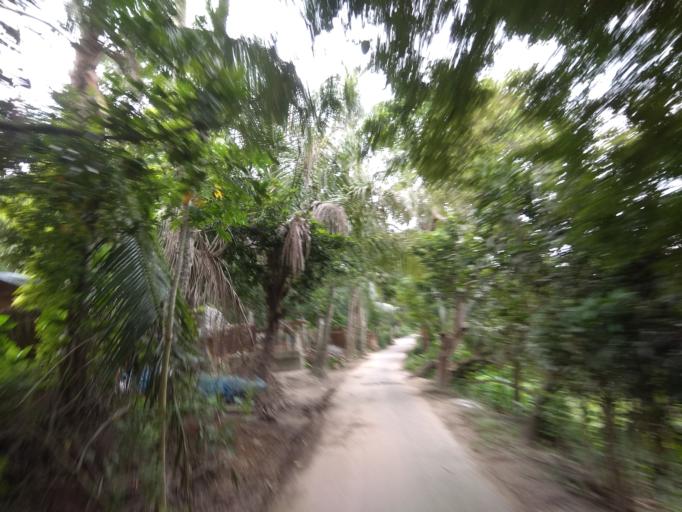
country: BD
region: Dhaka
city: Dohar
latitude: 23.4856
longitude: 89.9984
